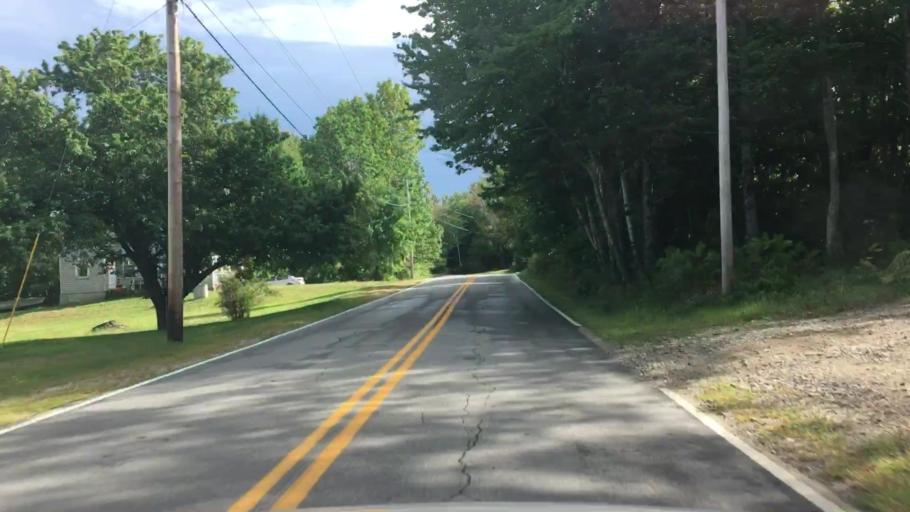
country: US
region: Maine
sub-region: Hancock County
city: Trenton
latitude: 44.4340
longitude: -68.3979
